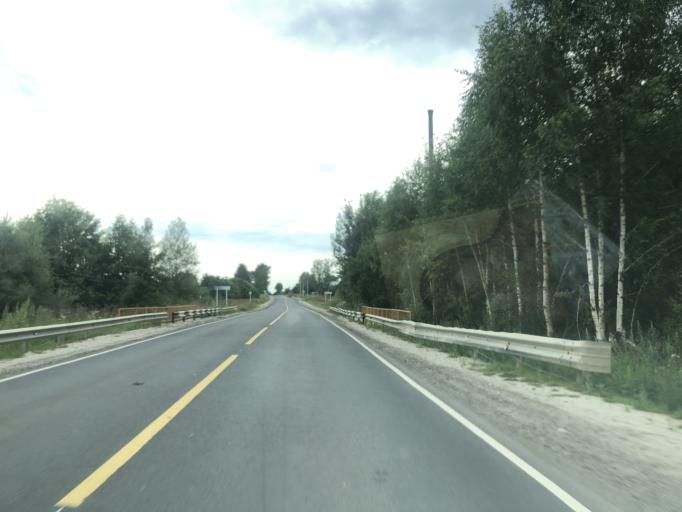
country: RU
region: Ivanovo
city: Pestyaki
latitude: 56.7053
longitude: 42.6943
